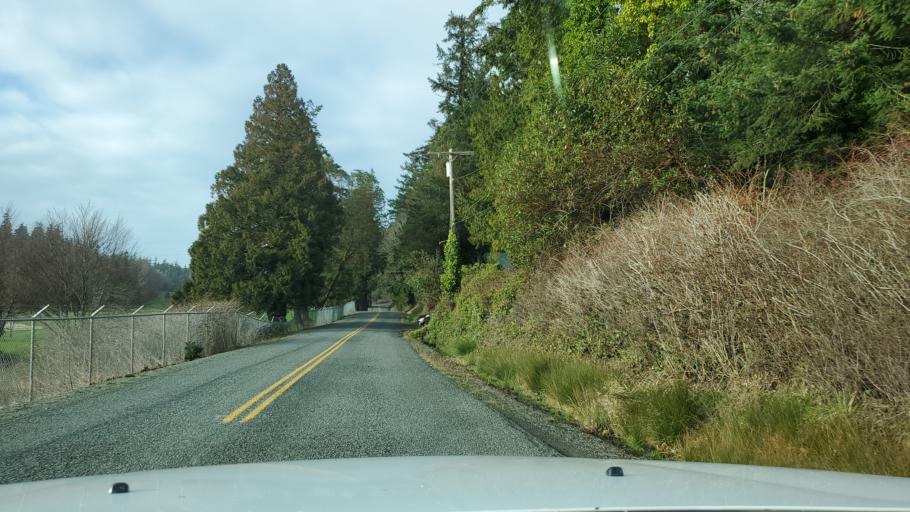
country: US
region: Washington
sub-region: Skagit County
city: Anacortes
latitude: 48.4499
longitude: -122.5739
